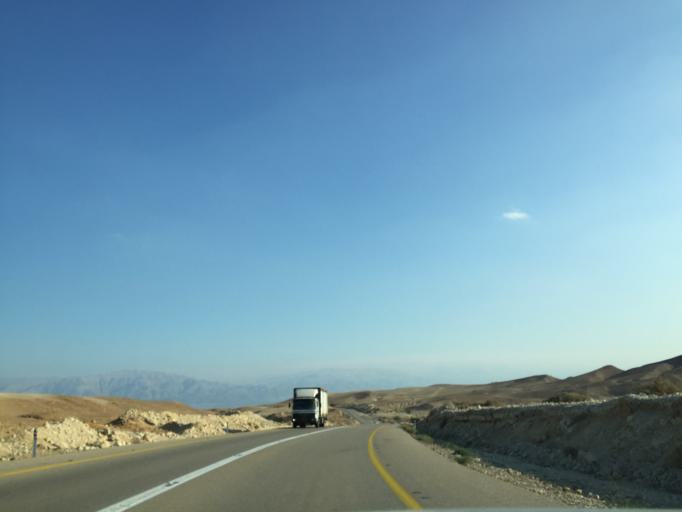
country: IL
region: Southern District
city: `En Boqeq
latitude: 31.1669
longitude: 35.3192
